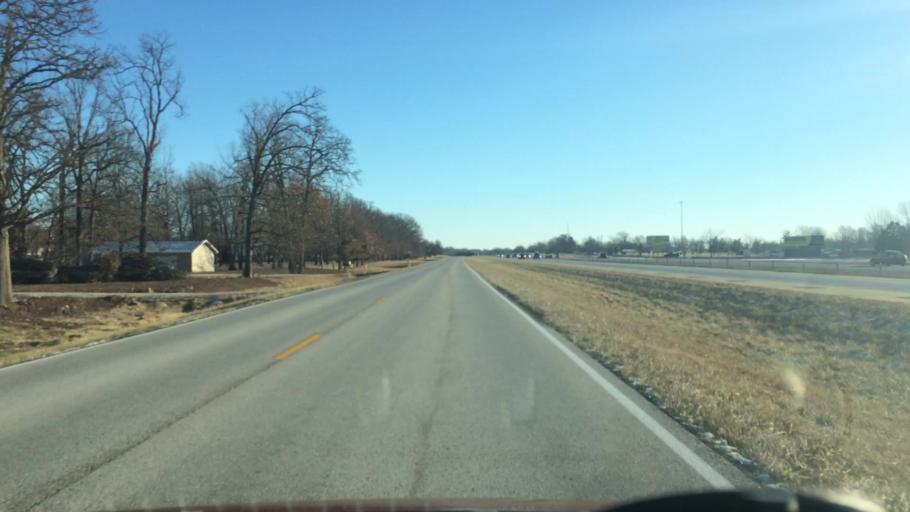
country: US
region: Missouri
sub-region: Greene County
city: Strafford
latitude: 37.2720
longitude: -93.0624
